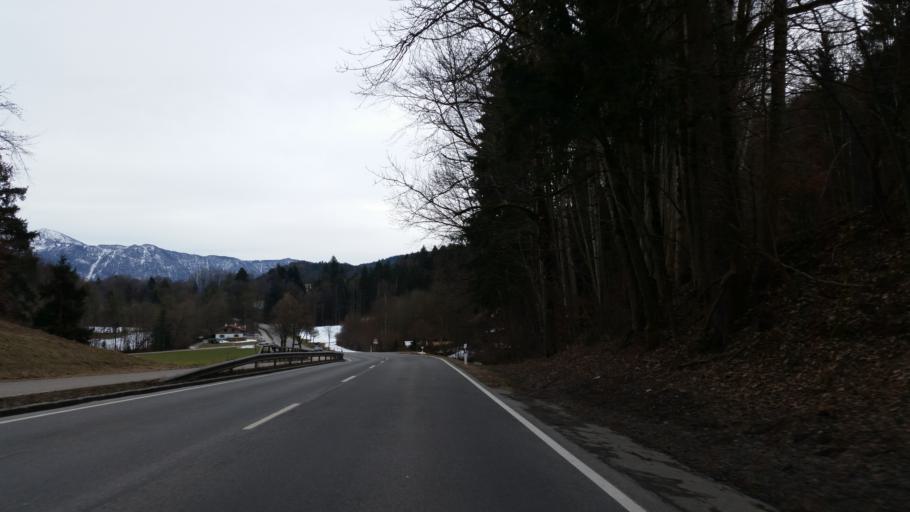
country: DE
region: Bavaria
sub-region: Upper Bavaria
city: Siegsdorf
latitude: 47.8140
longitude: 12.6818
